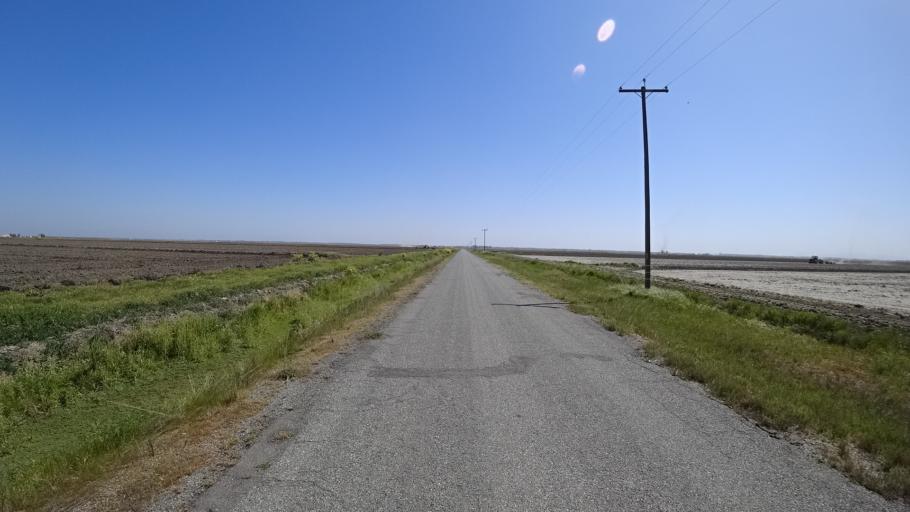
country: US
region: California
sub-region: Glenn County
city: Willows
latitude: 39.4929
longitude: -122.0776
